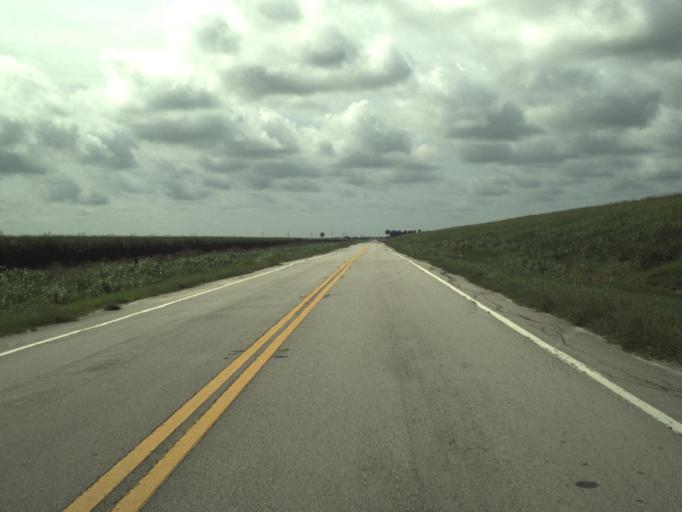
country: US
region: Florida
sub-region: Palm Beach County
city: Pahokee
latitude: 26.7658
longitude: -80.6885
